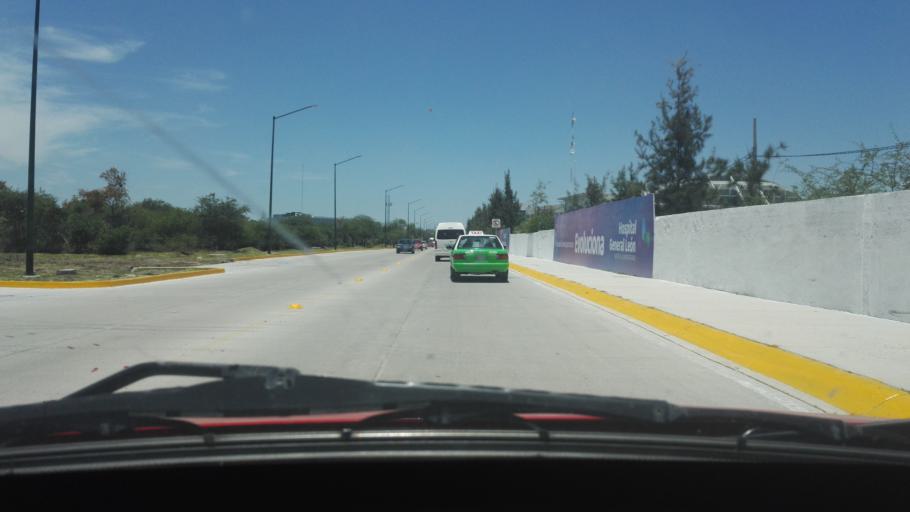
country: MX
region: Guanajuato
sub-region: Leon
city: Ladrilleras del Refugio
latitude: 21.0595
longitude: -101.5696
